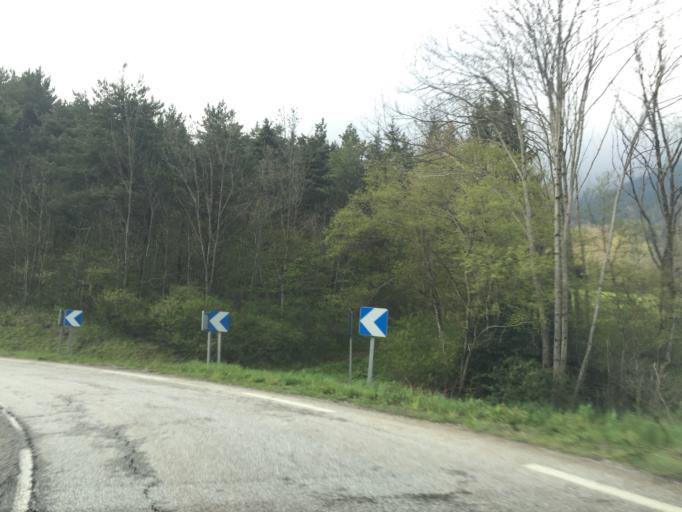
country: FR
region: Rhone-Alpes
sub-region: Departement de l'Isere
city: Mens
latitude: 44.7578
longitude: 5.6655
